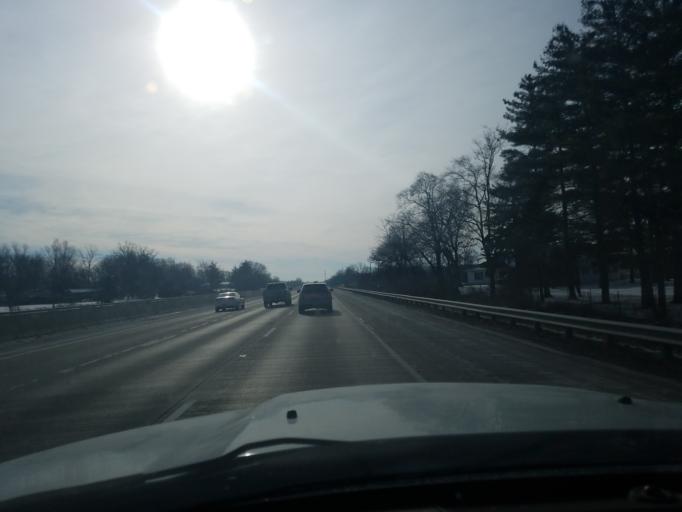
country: US
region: Indiana
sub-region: Allen County
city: Fort Wayne
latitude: 41.1002
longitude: -85.2096
